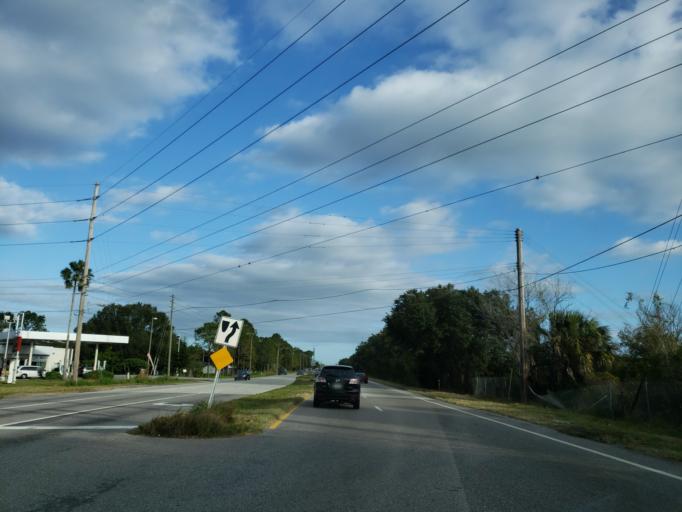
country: US
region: Florida
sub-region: Hillsborough County
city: Plant City
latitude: 28.0072
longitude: -82.1049
